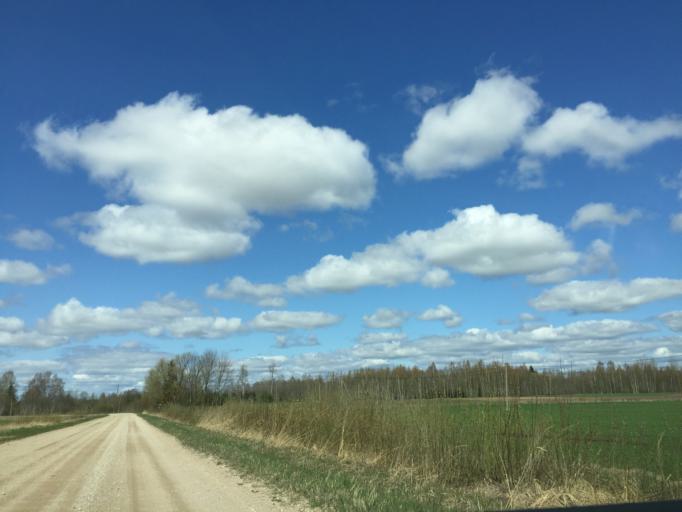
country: LV
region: Vilanu
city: Vilani
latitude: 56.6507
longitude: 27.1340
